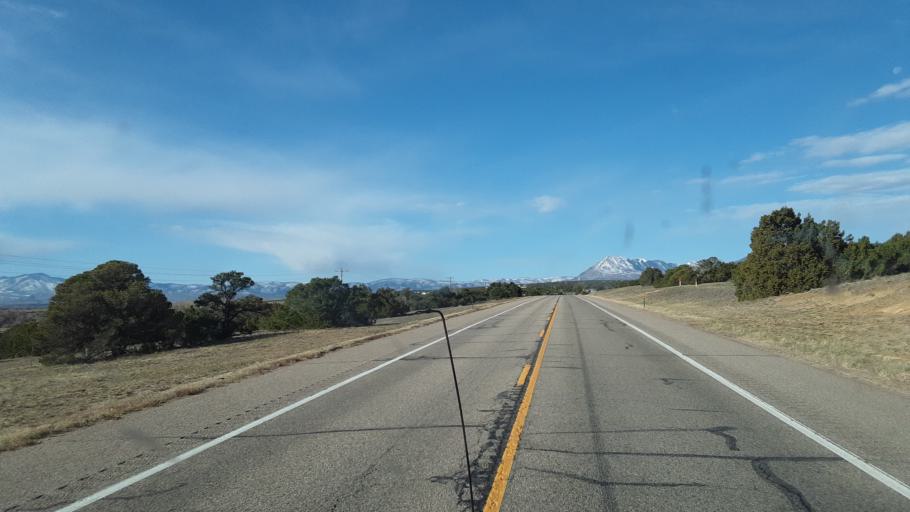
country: US
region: Colorado
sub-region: Huerfano County
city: Walsenburg
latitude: 37.5859
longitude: -104.8895
